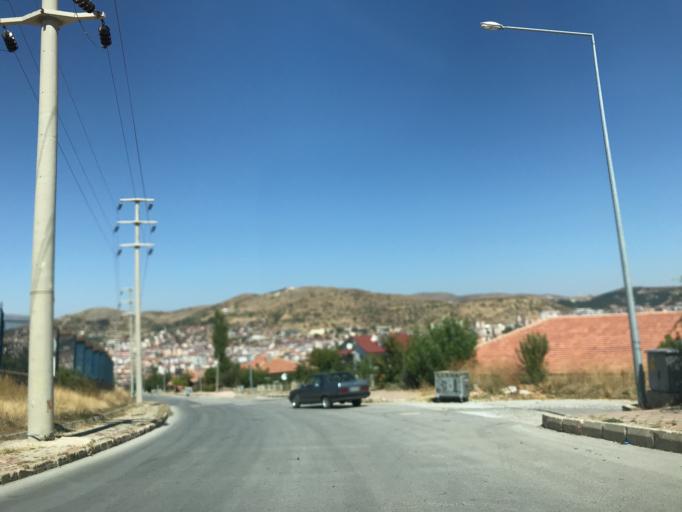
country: TR
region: Yozgat
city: Yozgat
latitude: 39.8153
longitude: 34.8226
